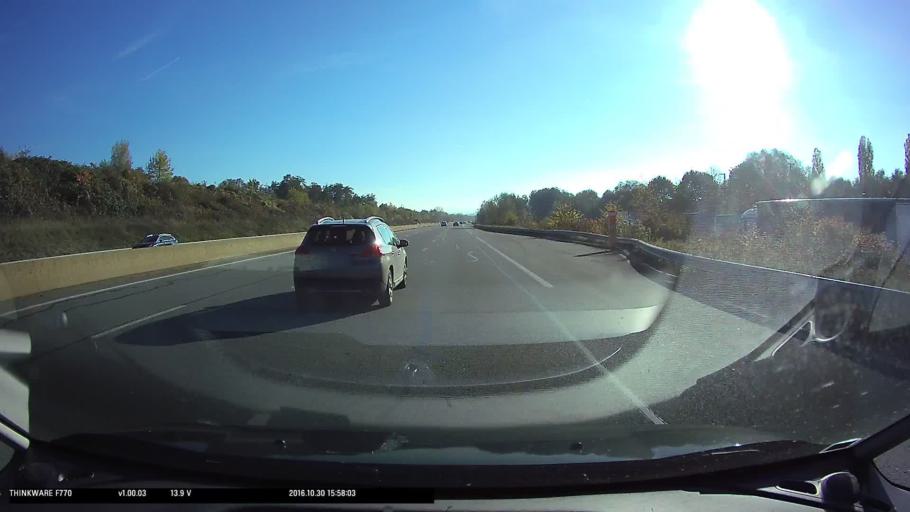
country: FR
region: Franche-Comte
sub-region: Departement du Doubs
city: Nommay
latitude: 47.5430
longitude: 6.8631
